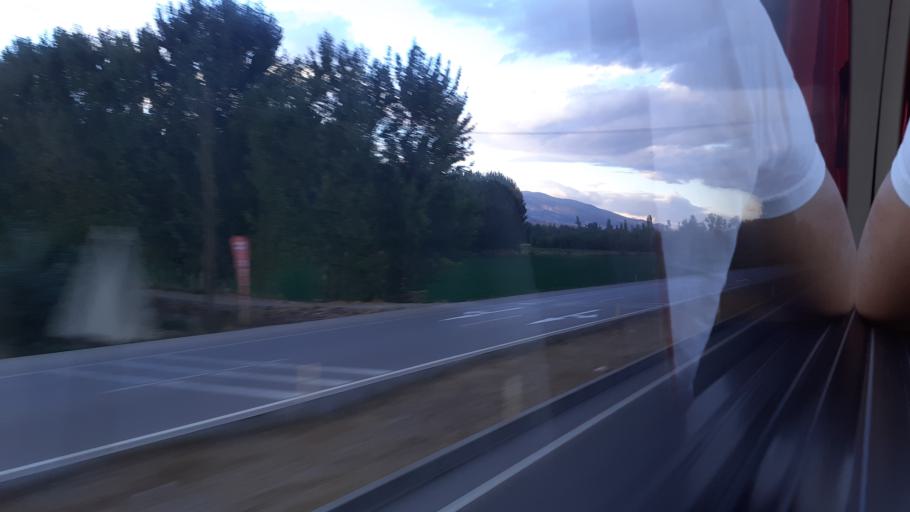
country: TR
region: Tokat
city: Dokmetepe
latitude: 40.3213
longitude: 36.2036
